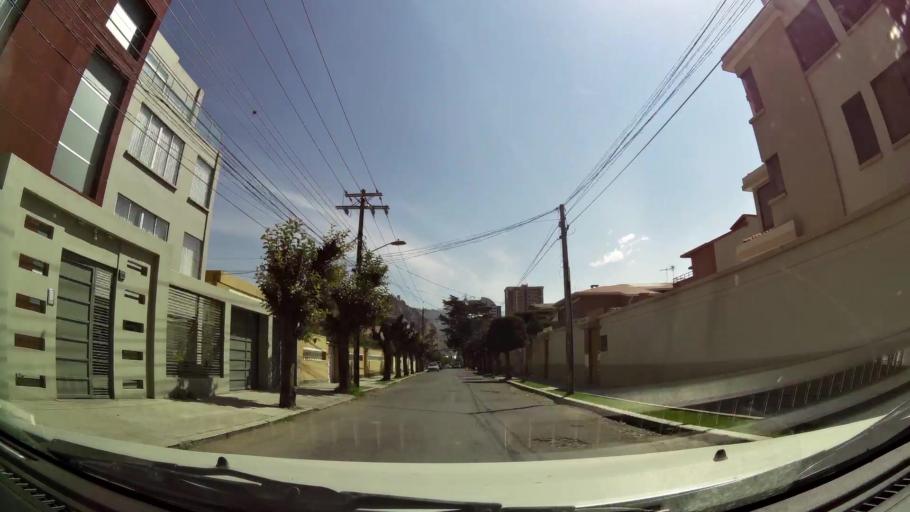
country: BO
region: La Paz
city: La Paz
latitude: -16.5431
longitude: -68.0854
